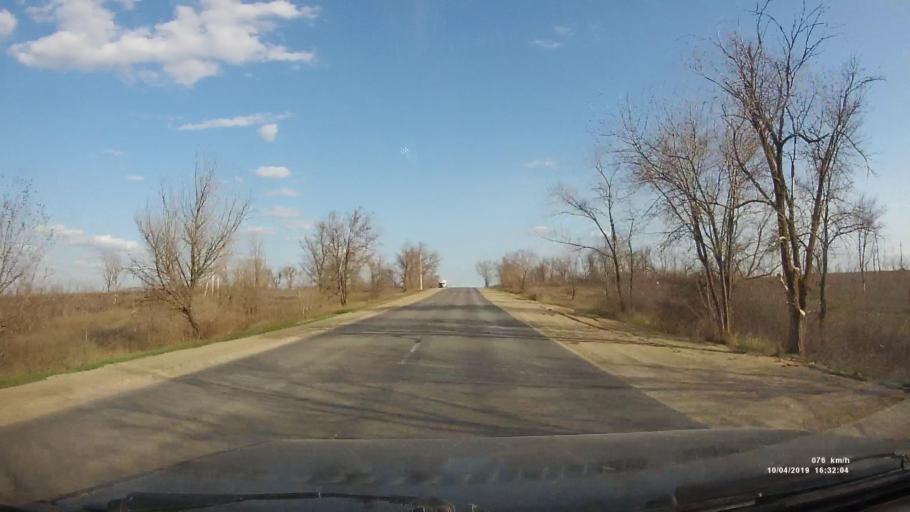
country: RU
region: Rostov
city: Staraya Stanitsa
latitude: 48.2491
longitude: 40.3830
